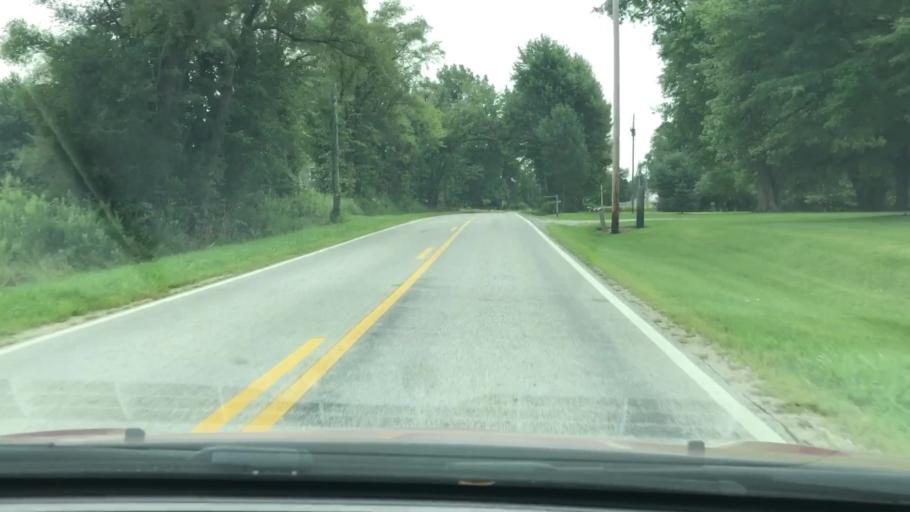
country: US
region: Ohio
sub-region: Delaware County
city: Sunbury
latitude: 40.2156
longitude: -82.8341
